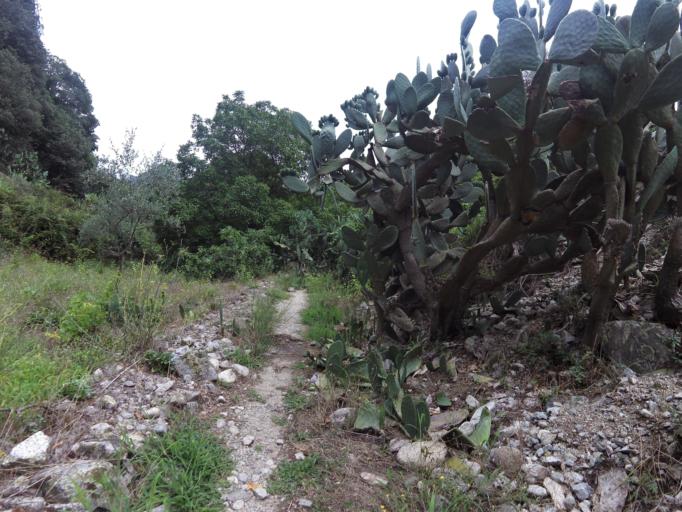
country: IT
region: Calabria
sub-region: Provincia di Reggio Calabria
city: Bivongi
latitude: 38.4867
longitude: 16.4295
